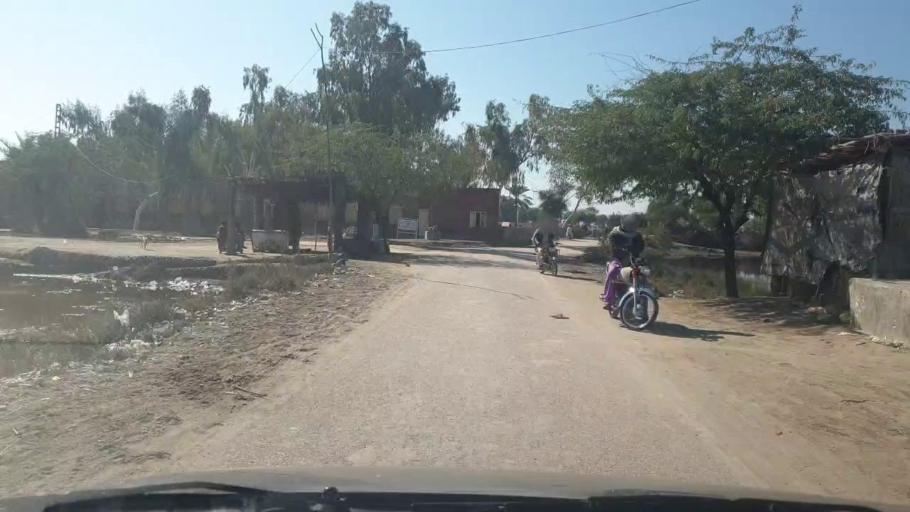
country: PK
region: Sindh
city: Bozdar
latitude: 27.1445
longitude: 68.6467
